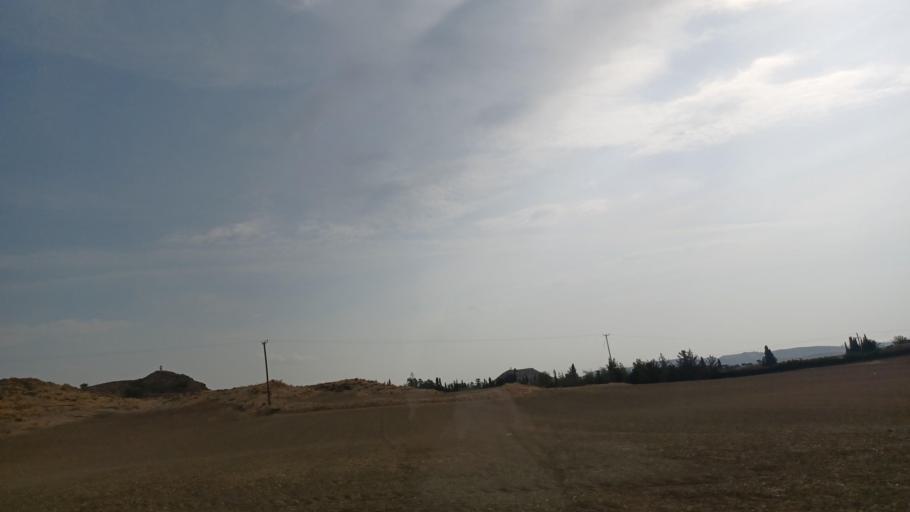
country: CY
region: Larnaka
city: Troulloi
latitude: 35.0121
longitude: 33.5767
